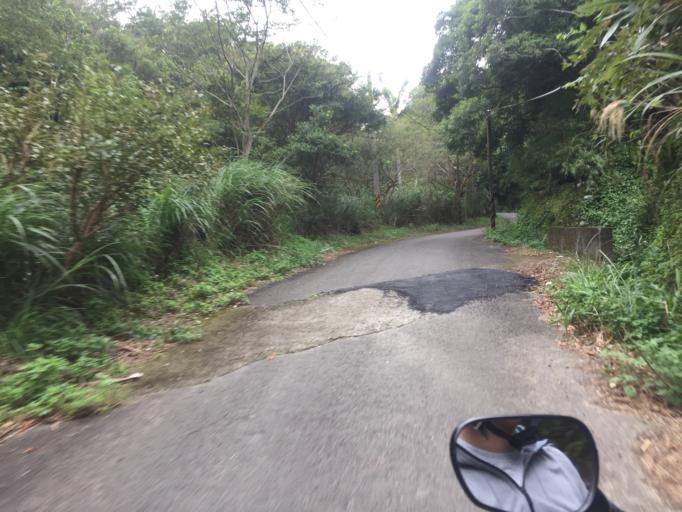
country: TW
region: Taiwan
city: Daxi
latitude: 24.7880
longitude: 121.1620
